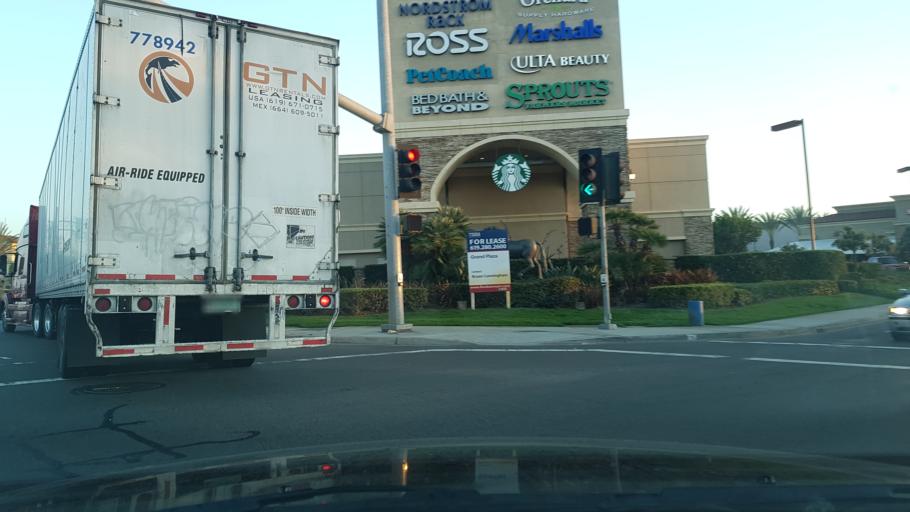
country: US
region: California
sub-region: San Diego County
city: Lake San Marcos
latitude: 33.1429
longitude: -117.1916
